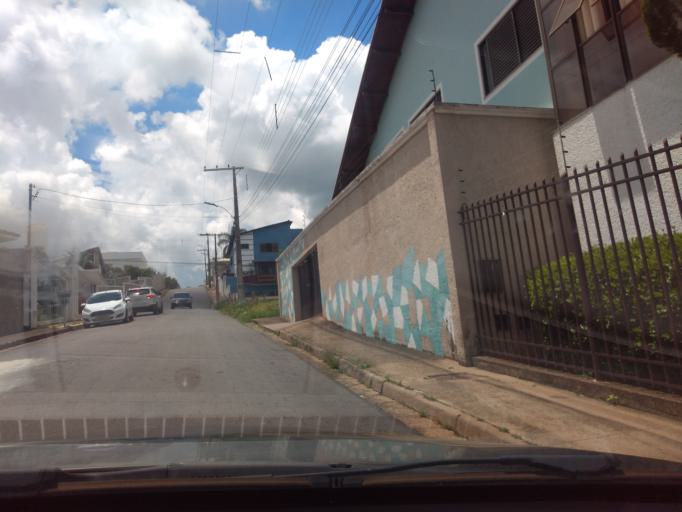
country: BR
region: Minas Gerais
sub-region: Tres Coracoes
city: Tres Coracoes
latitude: -21.6932
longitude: -45.2635
